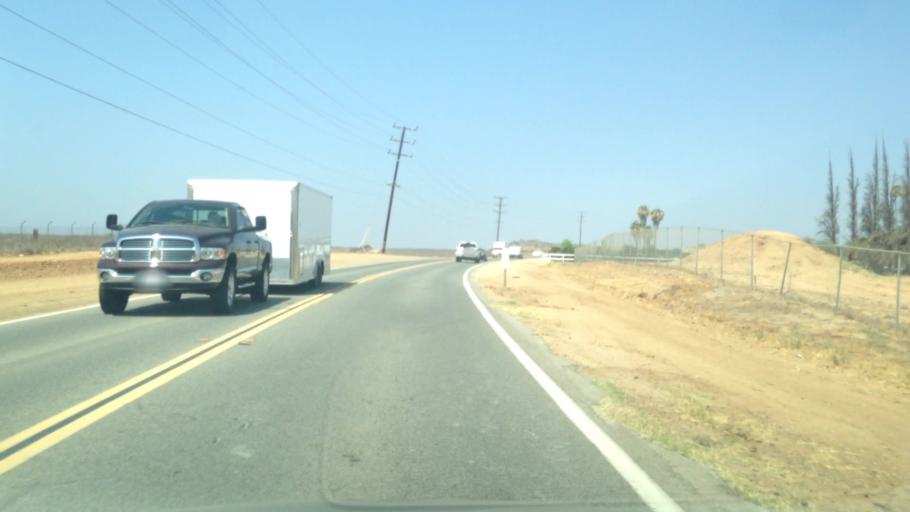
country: US
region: California
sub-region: Riverside County
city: Woodcrest
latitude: 33.8528
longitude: -117.3959
